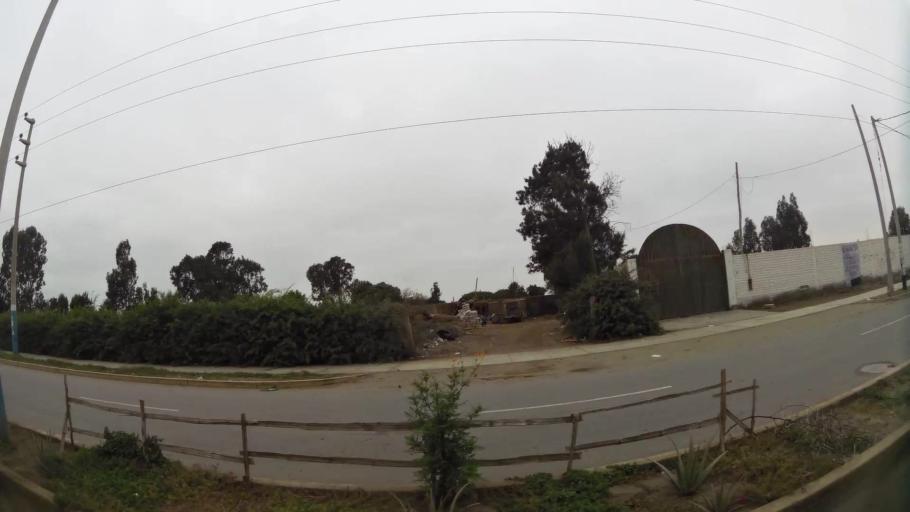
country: PE
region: Ica
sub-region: Provincia de Pisco
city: Pisco
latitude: -13.7260
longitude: -76.2032
